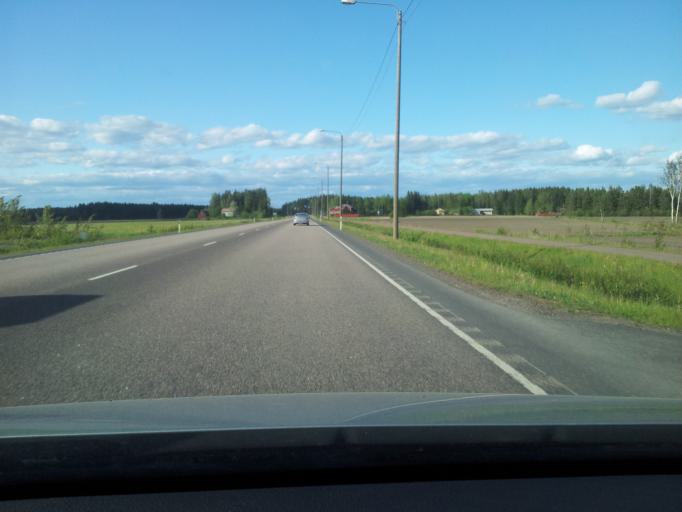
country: FI
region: Kymenlaakso
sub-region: Kouvola
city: Elimaeki
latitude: 60.8214
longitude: 26.5320
